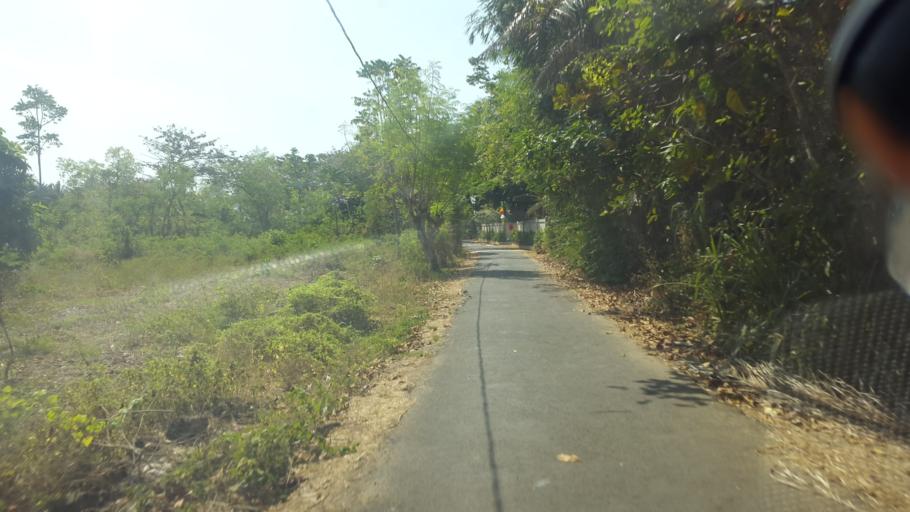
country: ID
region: West Java
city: Gunungbatu
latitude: -7.3384
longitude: 106.4009
